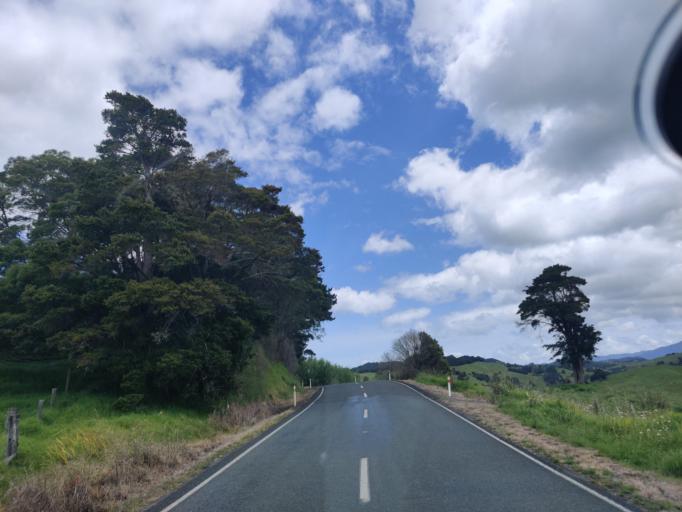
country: NZ
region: Northland
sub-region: Far North District
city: Kaitaia
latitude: -35.2825
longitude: 173.4849
